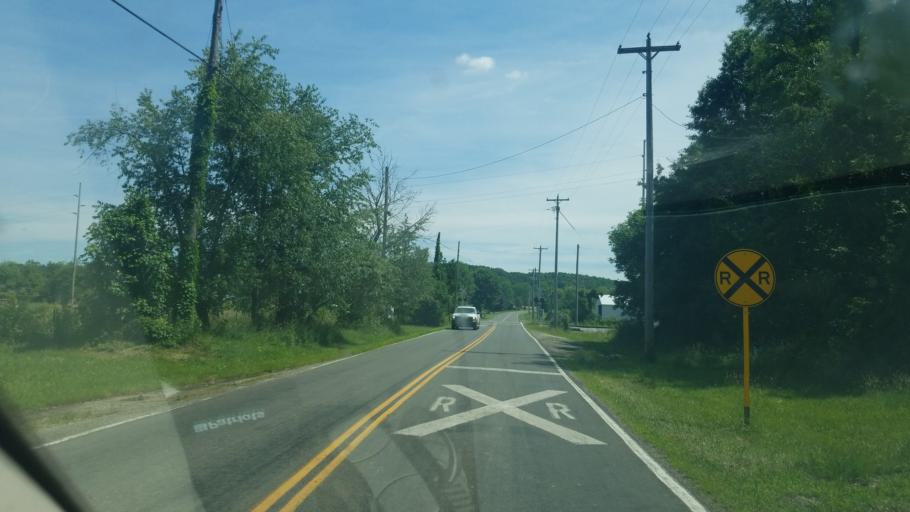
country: US
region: Ohio
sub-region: Stark County
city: Brewster
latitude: 40.7135
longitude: -81.5733
